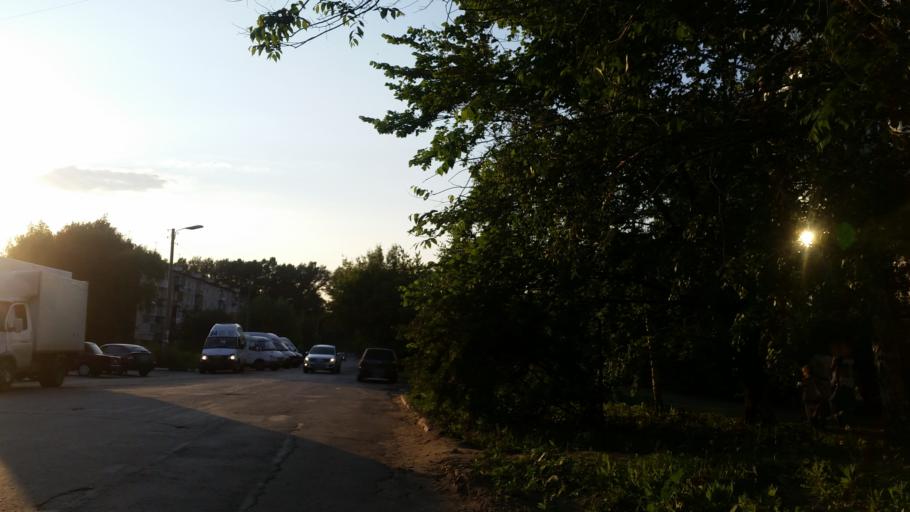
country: RU
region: Ulyanovsk
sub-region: Ulyanovskiy Rayon
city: Ulyanovsk
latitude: 54.3578
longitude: 48.3822
